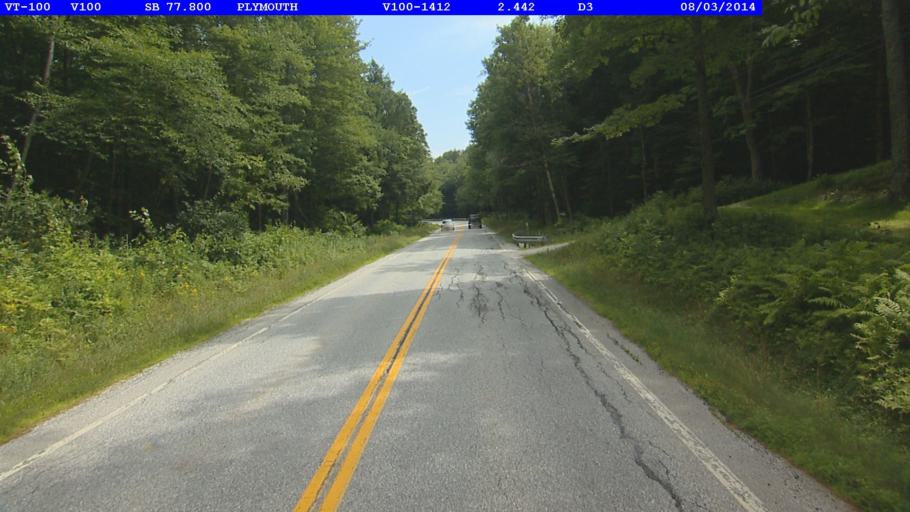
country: US
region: Vermont
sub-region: Windsor County
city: Woodstock
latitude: 43.4963
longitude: -72.7127
